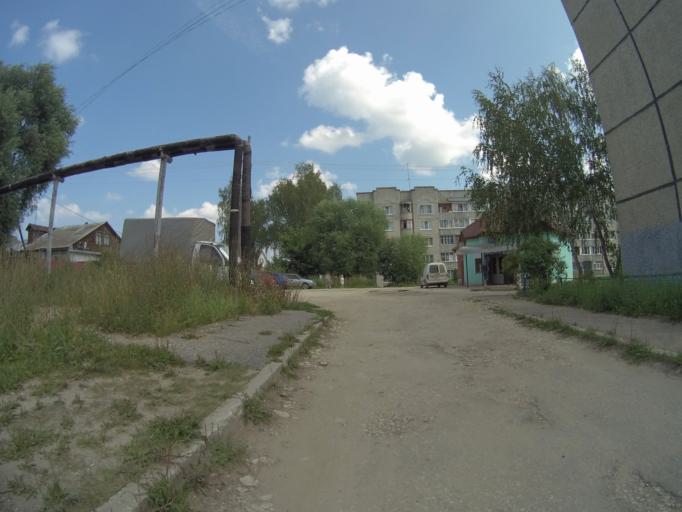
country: RU
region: Vladimir
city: Gus'-Khrustal'nyy
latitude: 55.6049
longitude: 40.6773
